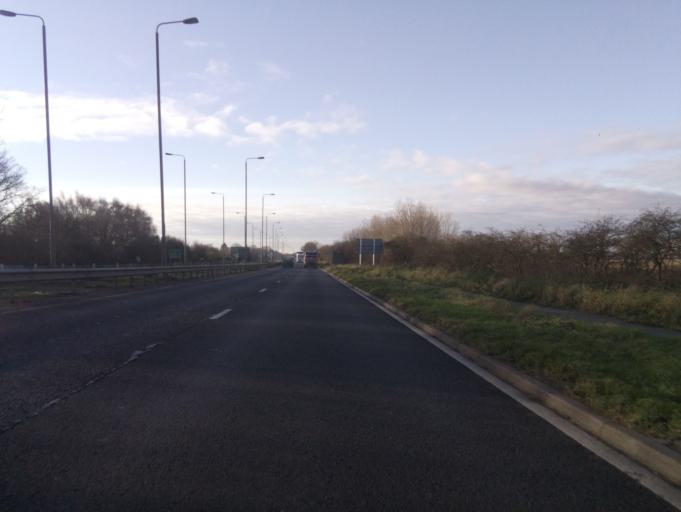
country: GB
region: England
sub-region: Derbyshire
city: Repton
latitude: 52.8587
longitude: -1.5780
